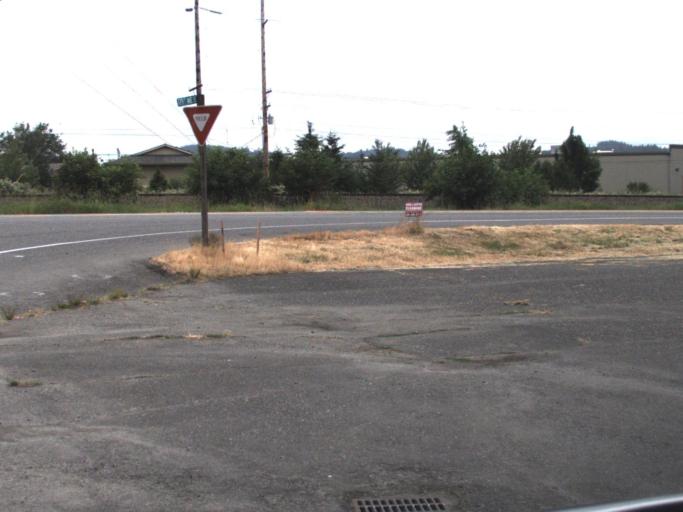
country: US
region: Washington
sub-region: Snohomish County
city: Everett
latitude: 47.9809
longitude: -122.1864
